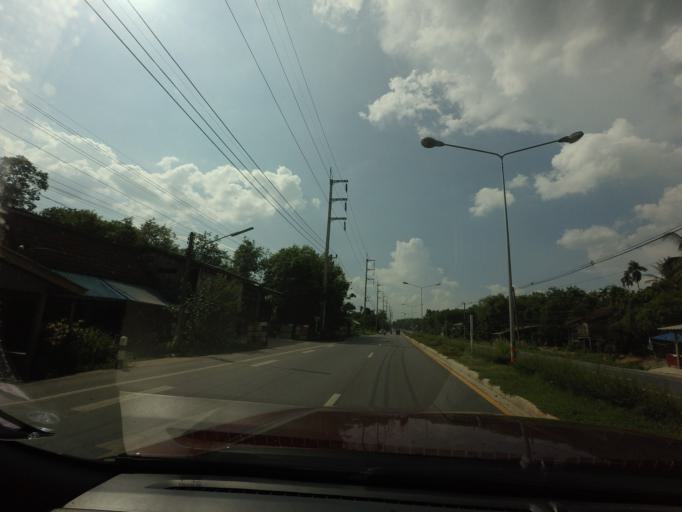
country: TH
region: Yala
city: Yala
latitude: 6.4855
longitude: 101.2652
